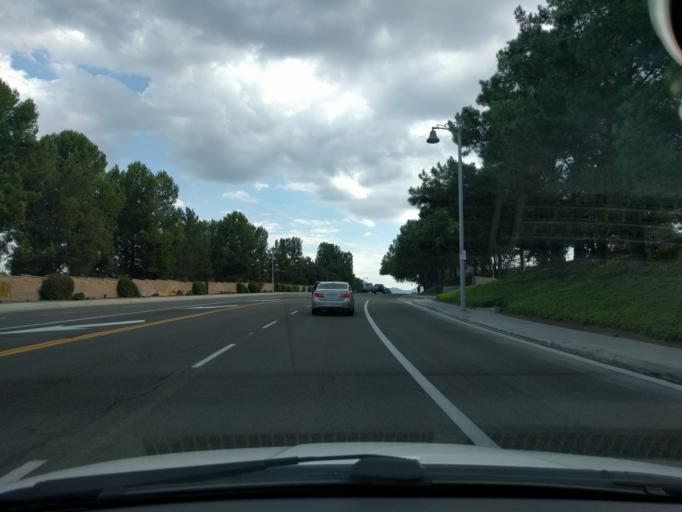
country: US
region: California
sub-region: Orange County
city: Las Flores
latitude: 33.6001
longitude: -117.6374
